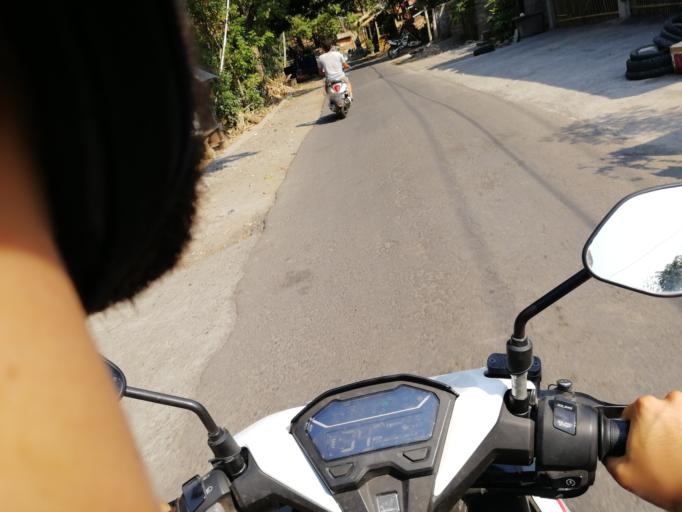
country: ID
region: Bali
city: Biaslantang Kaler
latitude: -8.3563
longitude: 115.6898
